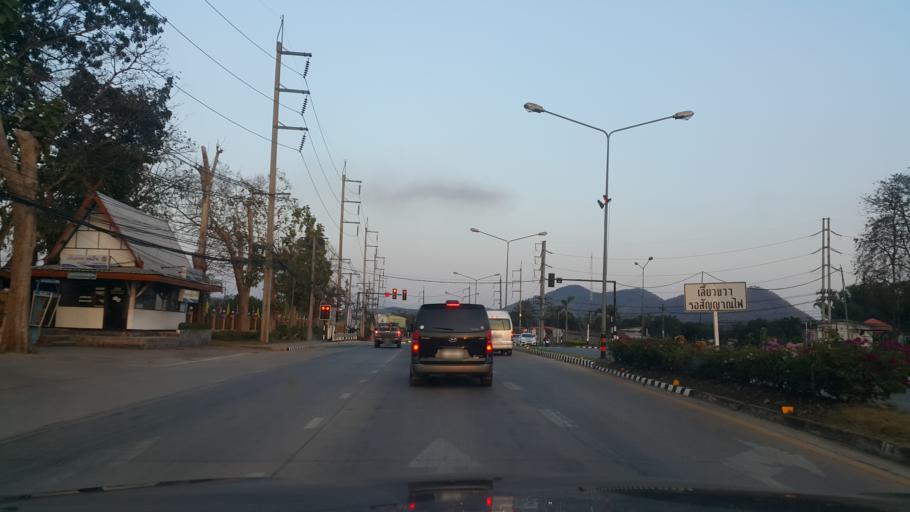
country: TH
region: Loei
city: Loei
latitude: 17.4955
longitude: 101.7196
